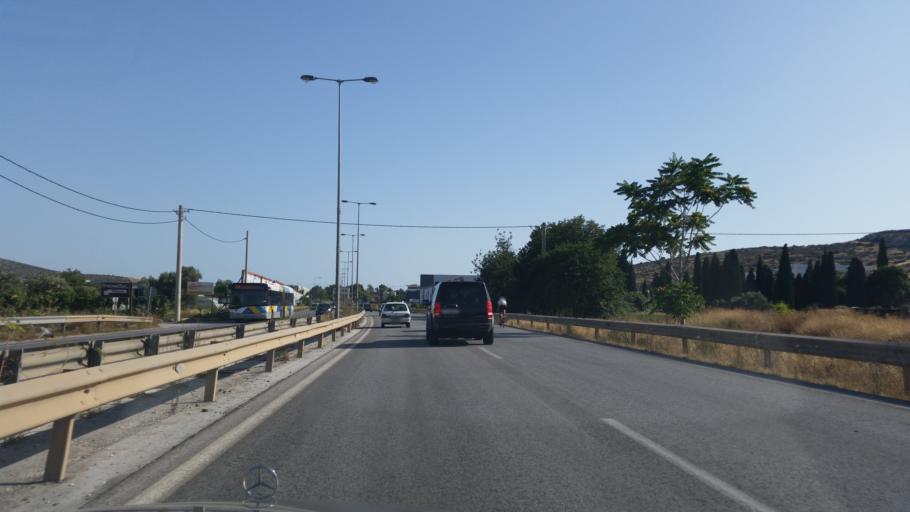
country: GR
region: Attica
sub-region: Nomarchia Anatolikis Attikis
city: Koropi
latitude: 37.8964
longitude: 23.8839
